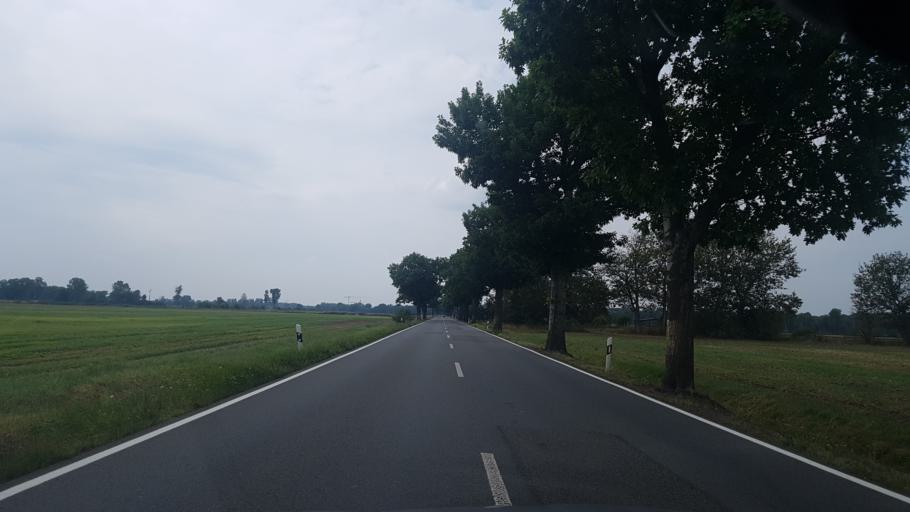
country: DE
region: Brandenburg
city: Schraden
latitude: 51.4692
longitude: 13.6700
